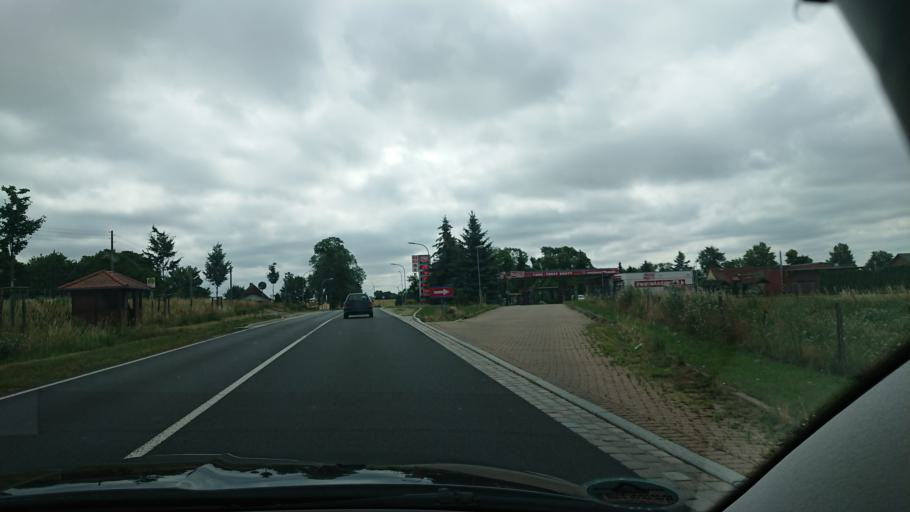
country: DE
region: Brandenburg
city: Plattenburg
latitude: 53.0019
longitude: 12.0622
